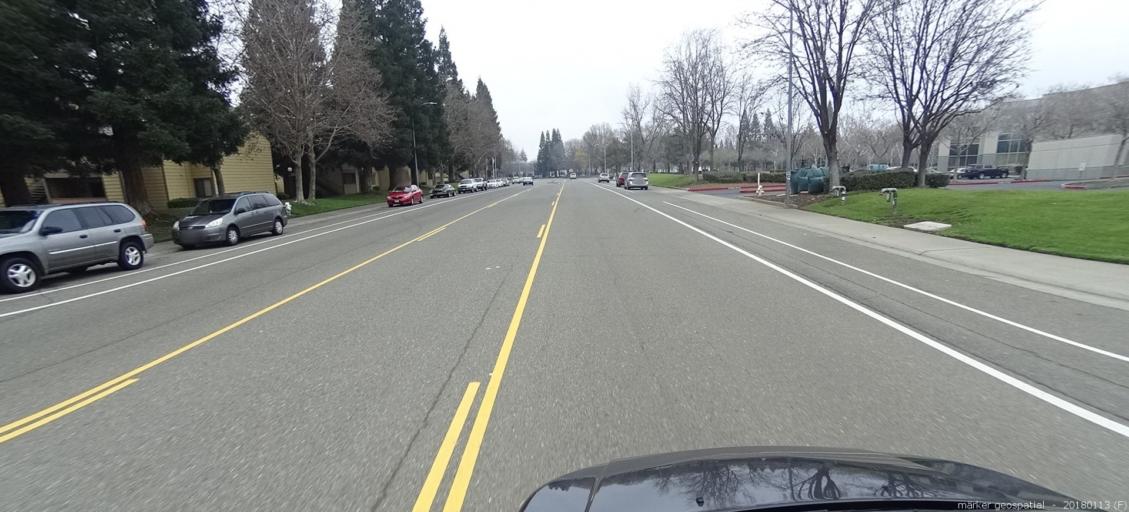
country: US
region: California
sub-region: Sacramento County
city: Rancho Cordova
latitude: 38.5825
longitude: -121.2922
